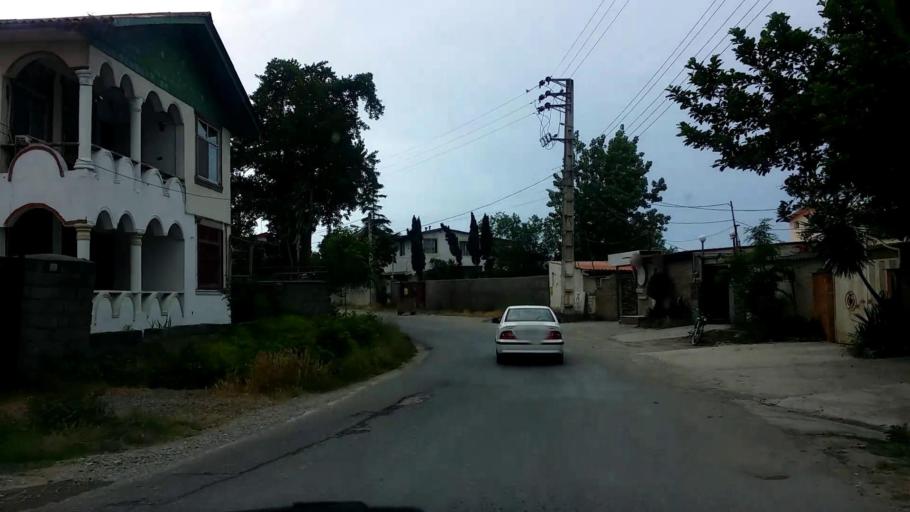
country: IR
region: Mazandaran
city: Chalus
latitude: 36.6857
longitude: 51.4146
